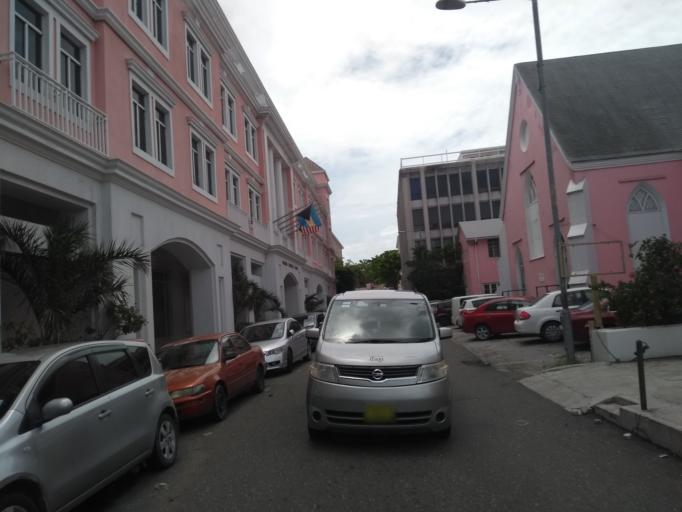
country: BS
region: New Providence
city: Nassau
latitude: 25.0771
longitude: -77.3419
